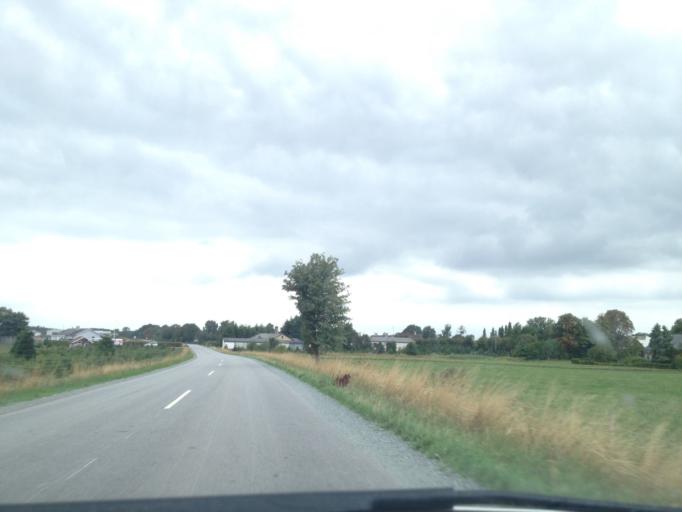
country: DK
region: South Denmark
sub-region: Kolding Kommune
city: Christiansfeld
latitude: 55.3072
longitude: 9.5117
